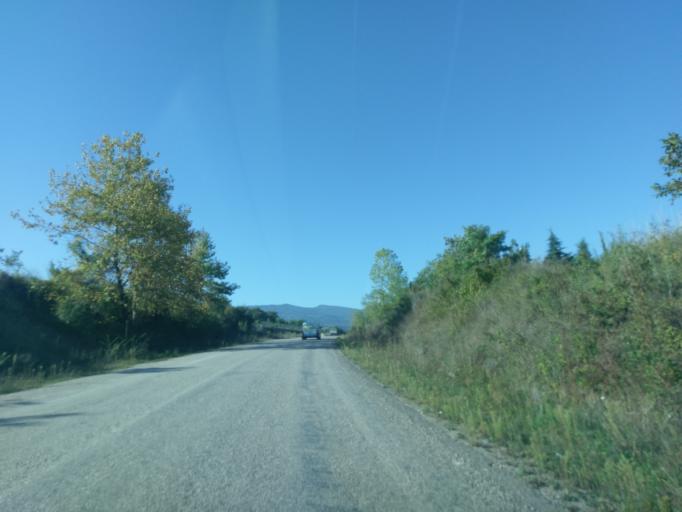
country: TR
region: Sinop
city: Kabali
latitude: 41.8475
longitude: 35.0601
